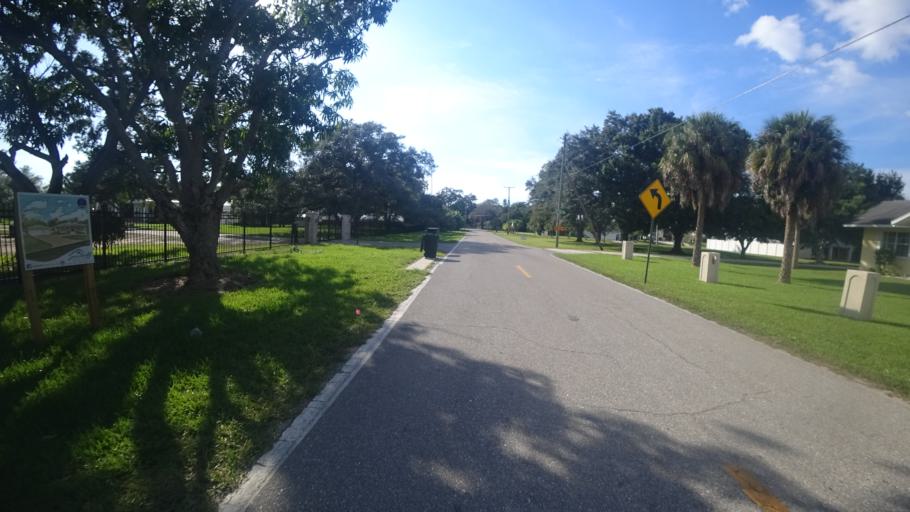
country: US
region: Florida
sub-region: Manatee County
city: West Bradenton
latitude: 27.5262
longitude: -82.6187
